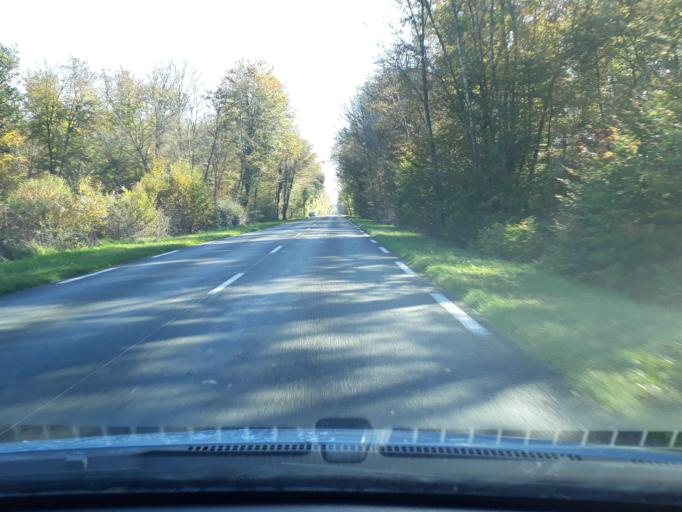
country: FR
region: Ile-de-France
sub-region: Departement de Seine-et-Marne
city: Bois-le-Roi
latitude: 48.4528
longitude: 2.7072
